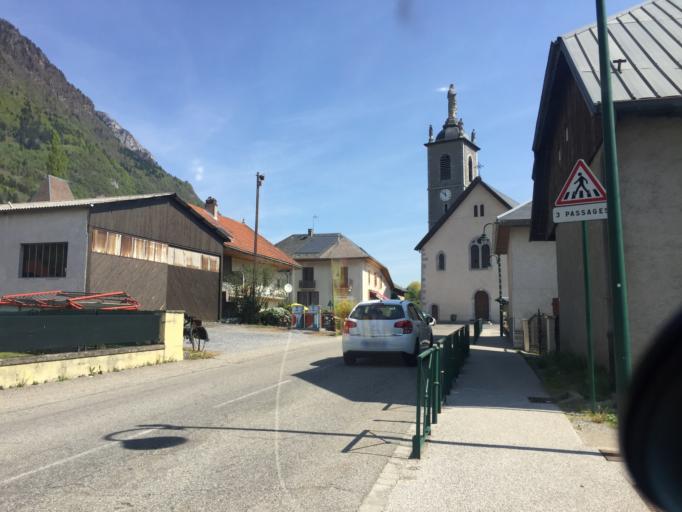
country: FR
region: Rhone-Alpes
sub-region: Departement de la Savoie
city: Mercury
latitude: 45.6739
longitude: 6.3367
